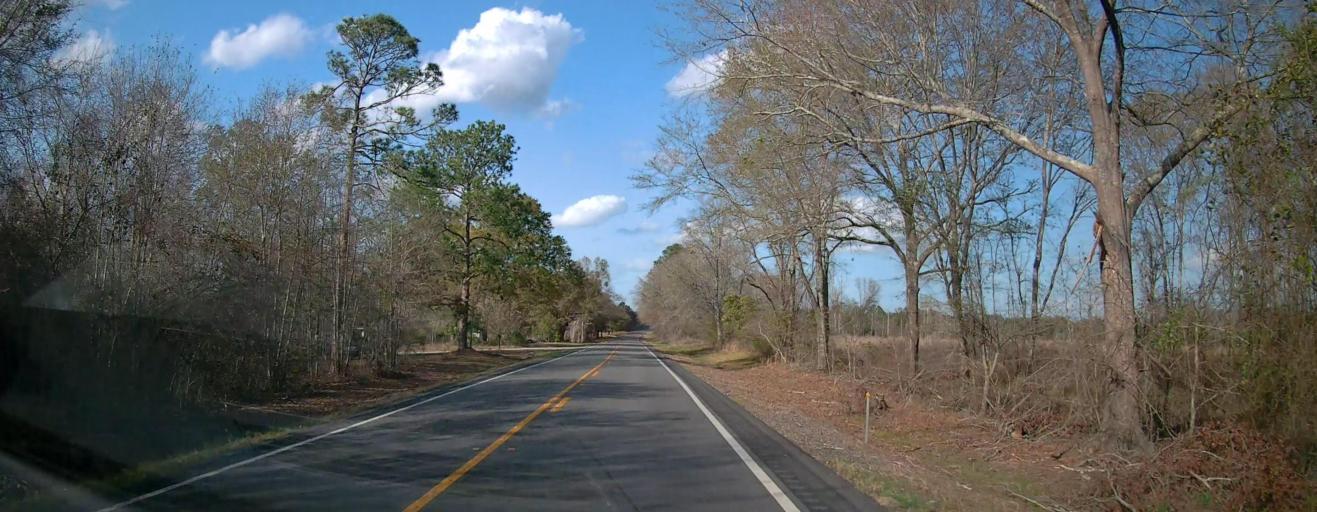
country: US
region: Georgia
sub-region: Wheeler County
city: Alamo
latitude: 32.0905
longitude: -82.8117
